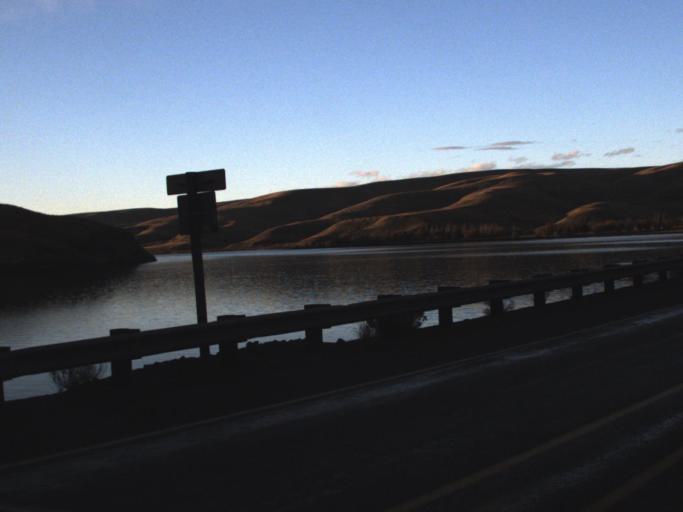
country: US
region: Washington
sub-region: Garfield County
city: Pomeroy
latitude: 46.6191
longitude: -117.7936
